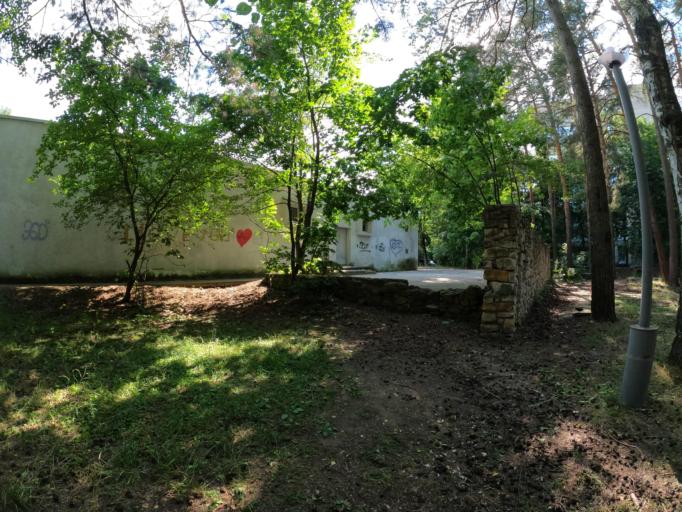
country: RU
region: Moskovskaya
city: Protvino
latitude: 54.8675
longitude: 37.2189
